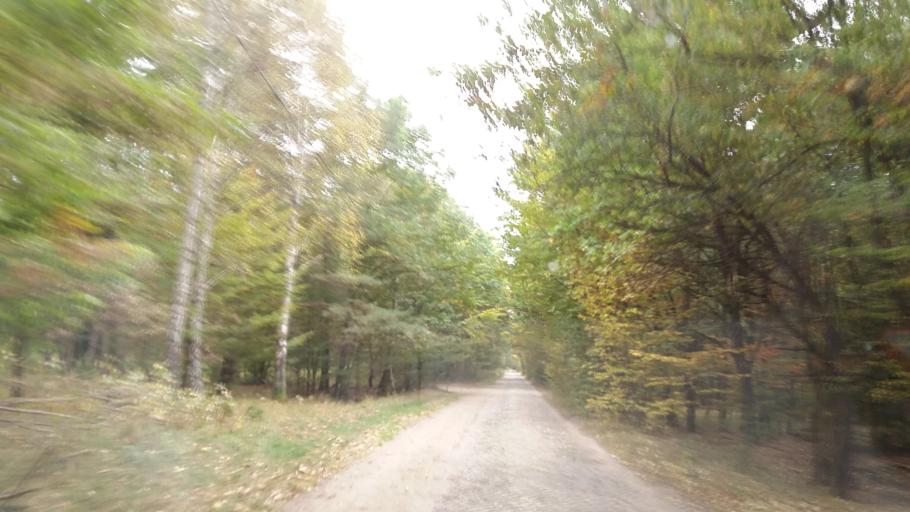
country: PL
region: West Pomeranian Voivodeship
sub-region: Powiat mysliborski
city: Barlinek
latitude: 52.9382
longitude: 15.2562
